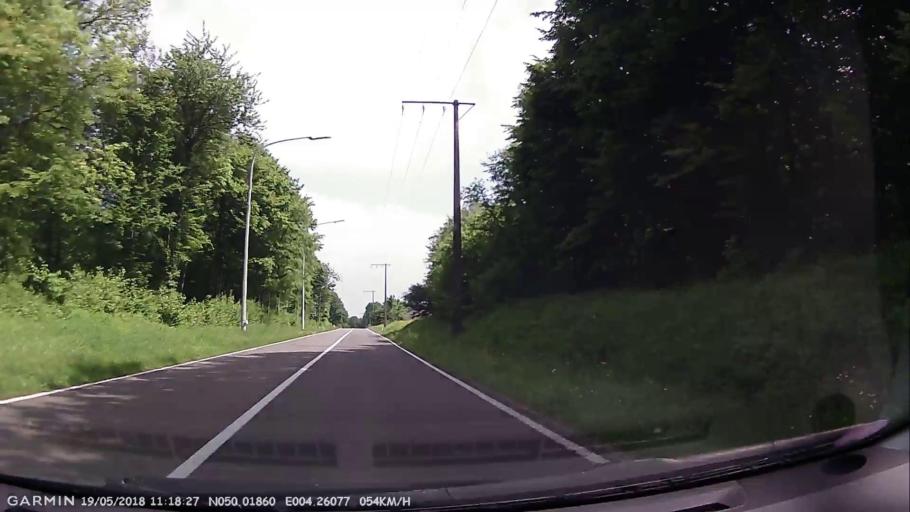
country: BE
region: Wallonia
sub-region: Province du Hainaut
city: Chimay
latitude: 50.0187
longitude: 4.2609
